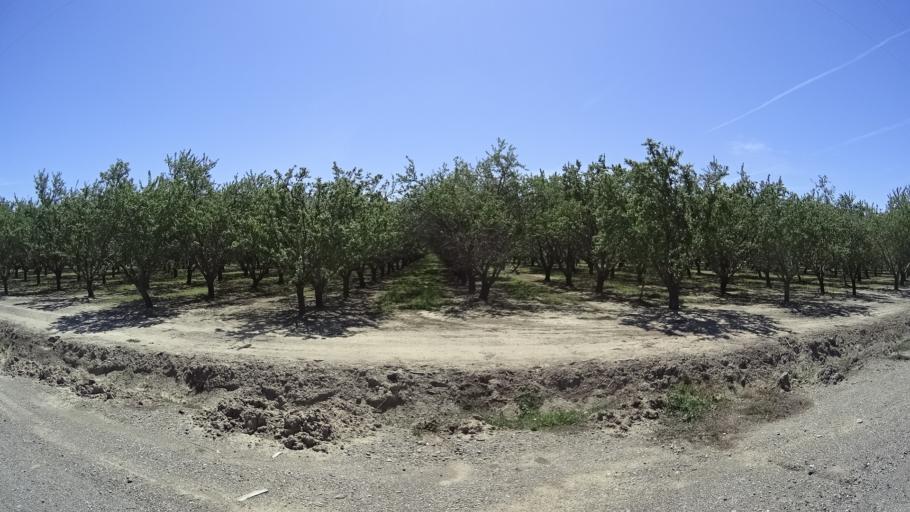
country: US
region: California
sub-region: Glenn County
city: Orland
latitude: 39.7251
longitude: -122.1305
